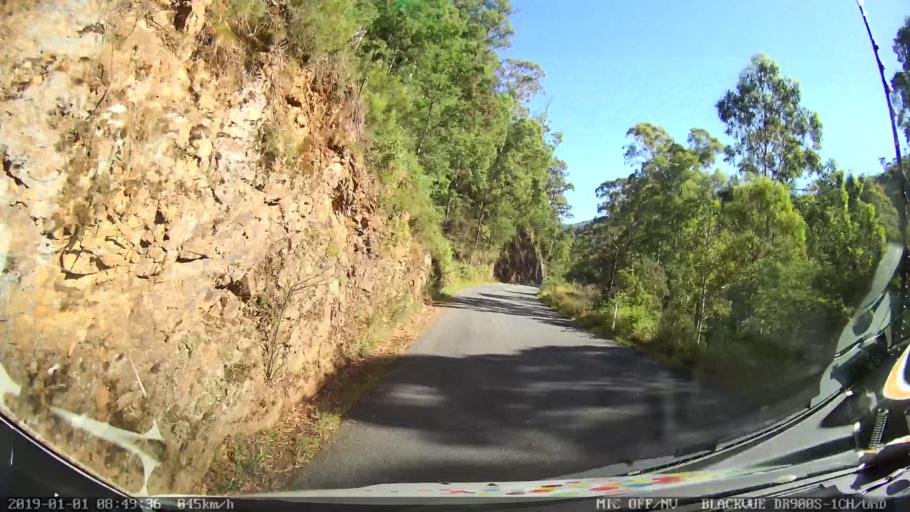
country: AU
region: New South Wales
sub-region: Snowy River
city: Jindabyne
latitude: -36.2815
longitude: 148.2007
